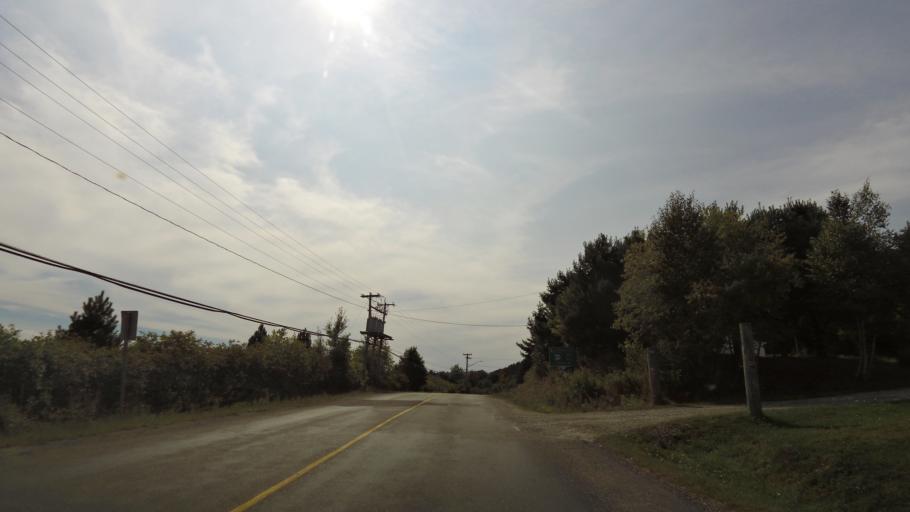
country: CA
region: New Brunswick
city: Hampton
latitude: 45.5375
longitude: -65.8626
